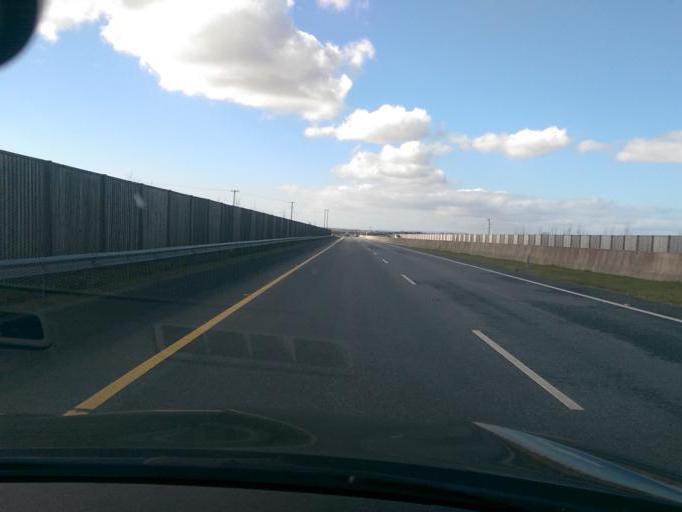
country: IE
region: Connaught
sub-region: County Galway
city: Oranmore
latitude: 53.2993
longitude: -8.8441
